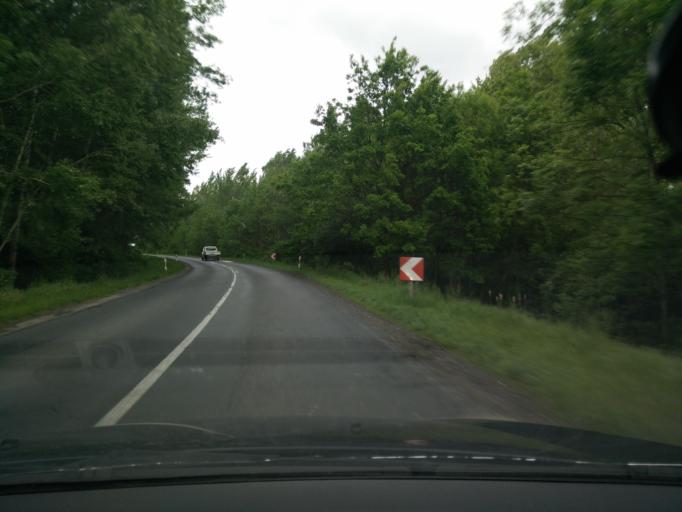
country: HU
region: Veszprem
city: Papa
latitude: 47.4067
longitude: 17.4729
